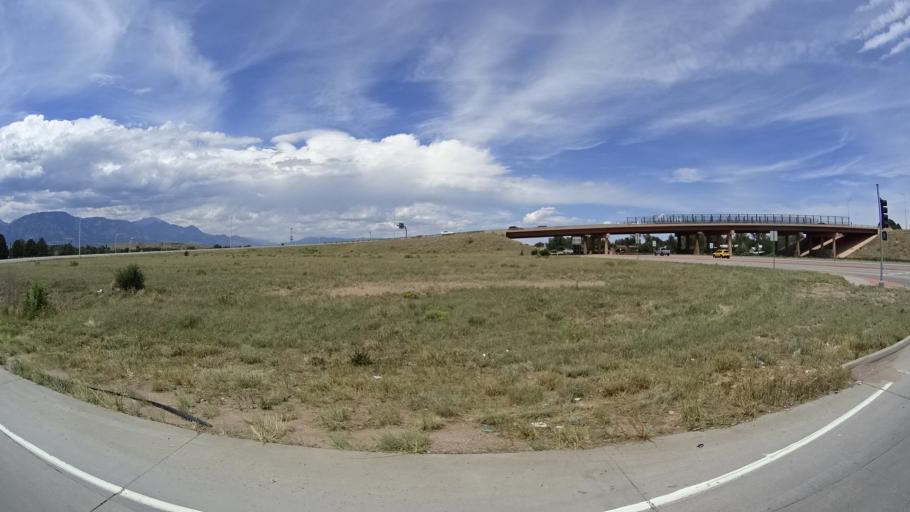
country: US
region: Colorado
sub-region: El Paso County
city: Security-Widefield
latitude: 38.7215
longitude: -104.7181
